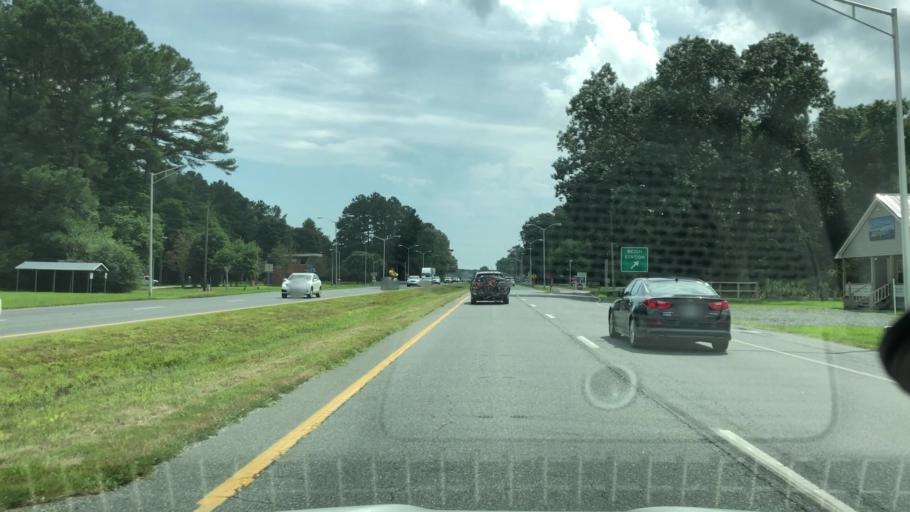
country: US
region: Virginia
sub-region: Accomack County
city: Wattsville
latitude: 37.9774
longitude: -75.5308
